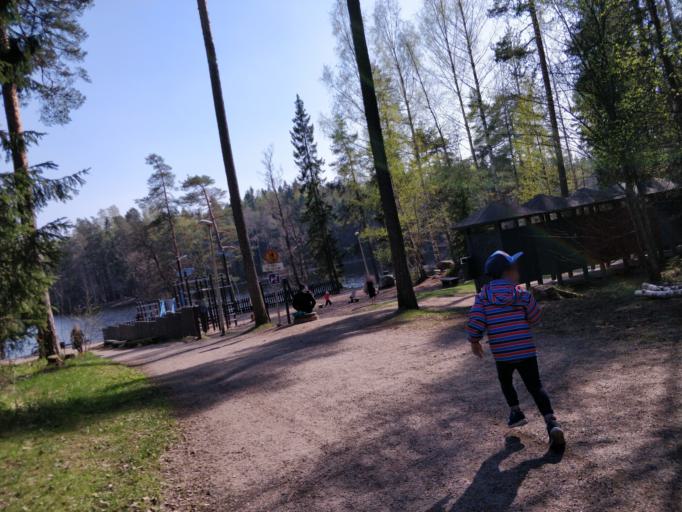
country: FI
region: Uusimaa
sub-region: Helsinki
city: Vantaa
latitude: 60.3139
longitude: 25.1123
